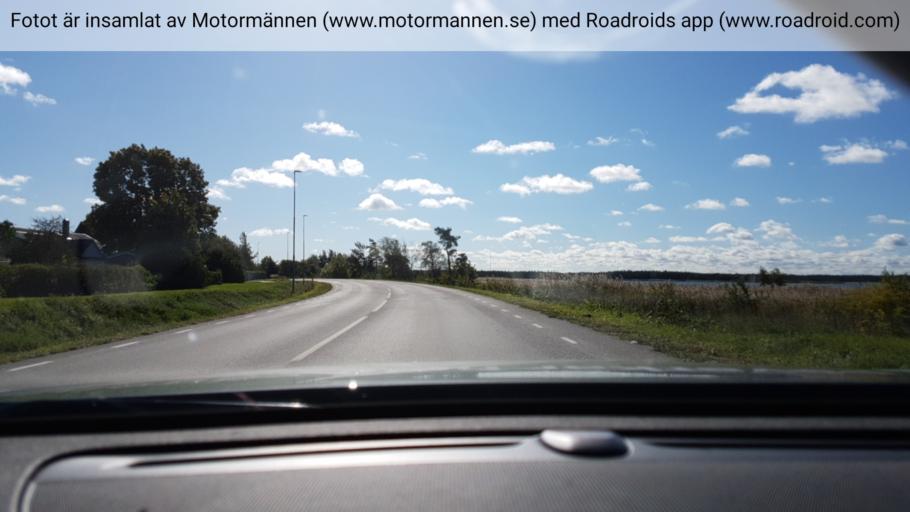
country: SE
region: Gotland
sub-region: Gotland
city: Slite
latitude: 57.7005
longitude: 18.7950
